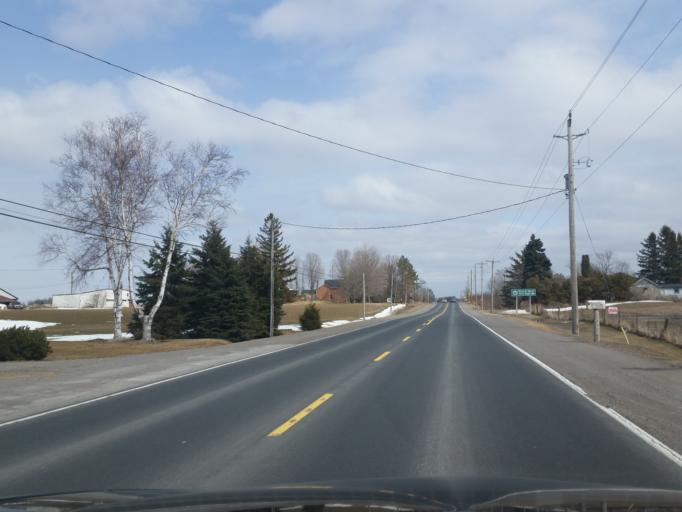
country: CA
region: Ontario
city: Cobourg
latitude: 43.9612
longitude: -78.3972
